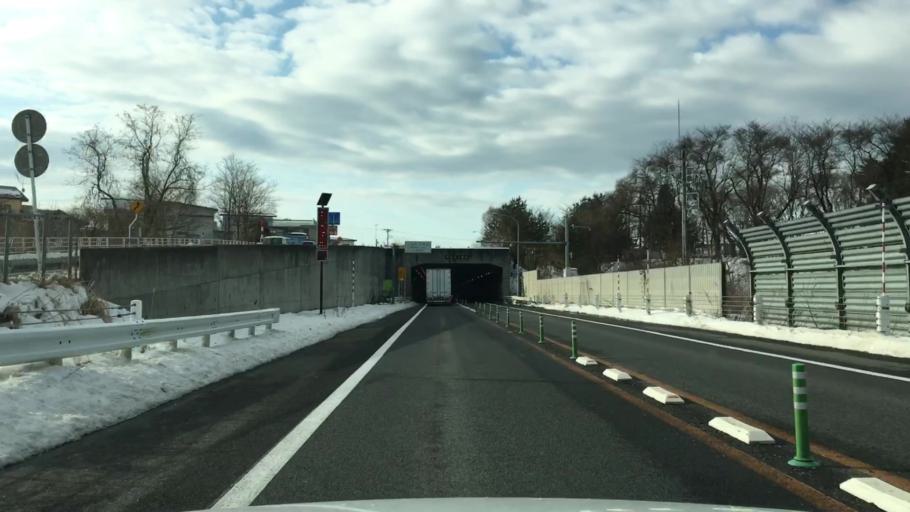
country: JP
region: Akita
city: Odate
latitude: 40.2775
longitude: 140.5360
